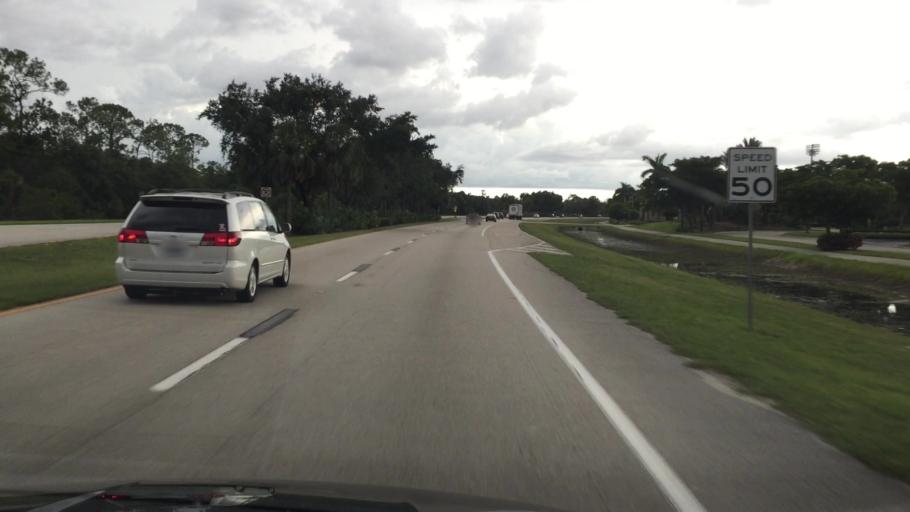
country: US
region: Florida
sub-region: Lee County
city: Villas
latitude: 26.5416
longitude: -81.8397
